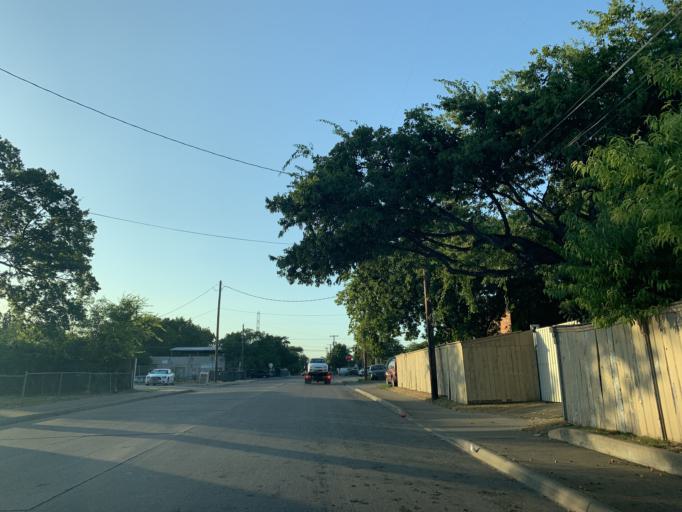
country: US
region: Texas
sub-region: Dallas County
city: Dallas
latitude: 32.7006
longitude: -96.8056
